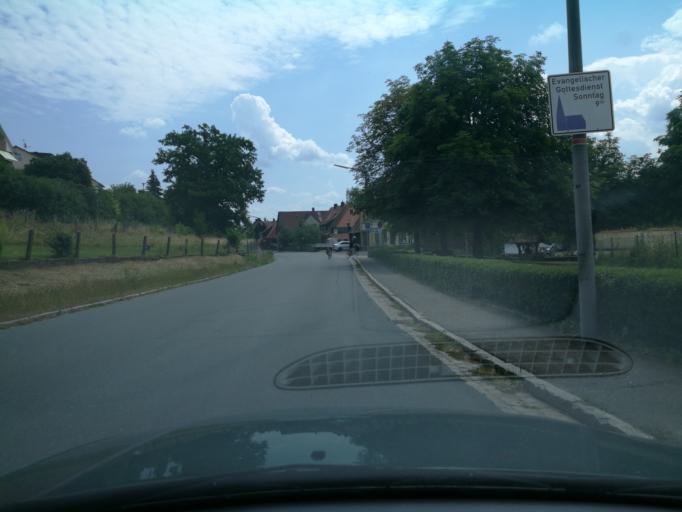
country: DE
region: Bavaria
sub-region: Regierungsbezirk Mittelfranken
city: Grosshabersdorf
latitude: 49.4074
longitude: 10.7815
